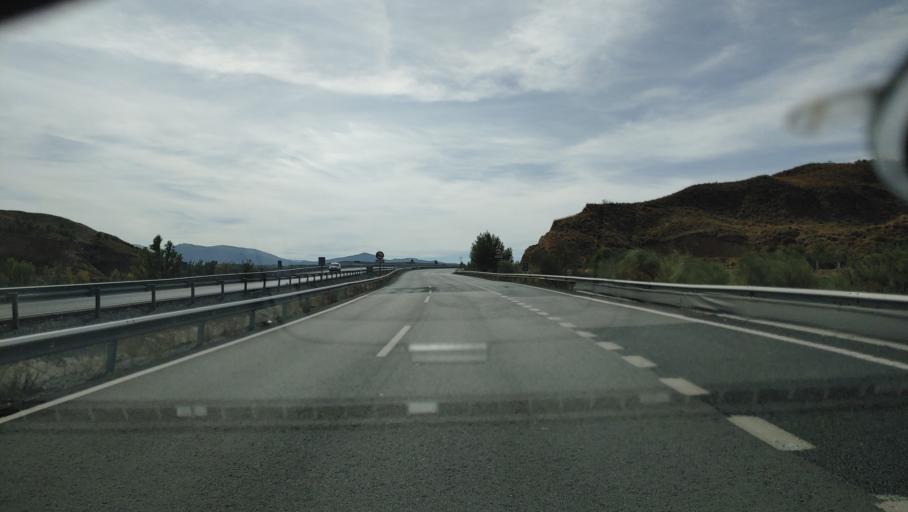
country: ES
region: Andalusia
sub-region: Provincia de Granada
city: Purullena
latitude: 37.3300
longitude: -3.2250
